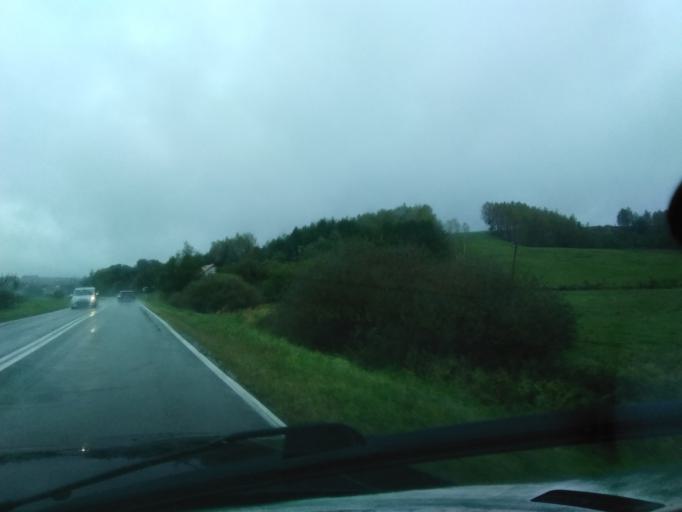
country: PL
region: Subcarpathian Voivodeship
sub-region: Powiat ropczycko-sedziszowski
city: Niedzwiada
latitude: 49.9840
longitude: 21.5603
